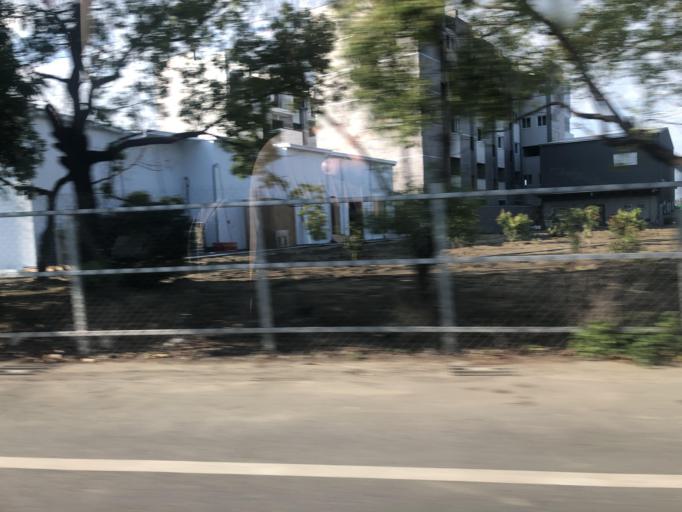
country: TW
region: Taiwan
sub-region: Tainan
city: Tainan
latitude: 23.0301
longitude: 120.1966
